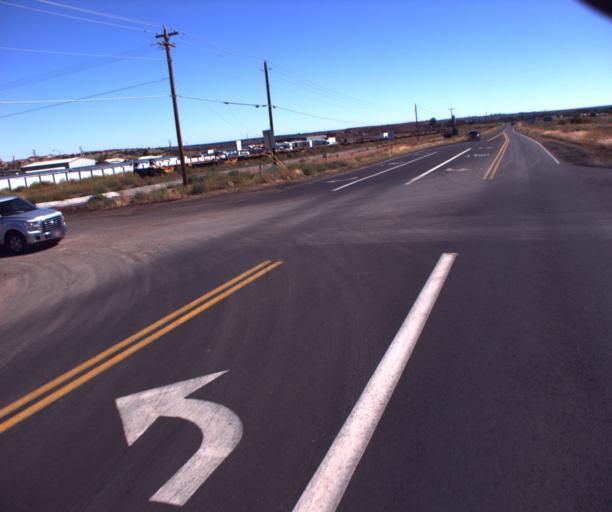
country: US
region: Arizona
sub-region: Navajo County
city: Snowflake
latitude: 34.5131
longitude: -110.1050
